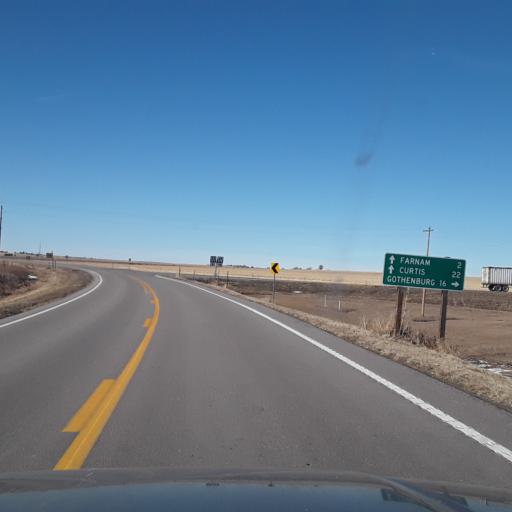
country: US
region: Nebraska
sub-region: Dawson County
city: Gothenburg
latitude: 40.7030
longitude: -100.1668
